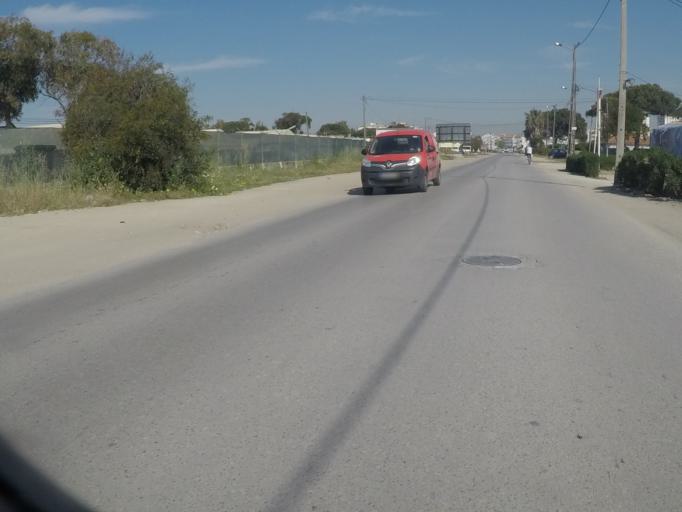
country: PT
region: Setubal
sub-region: Almada
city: Costa de Caparica
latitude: 38.6341
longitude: -9.2262
